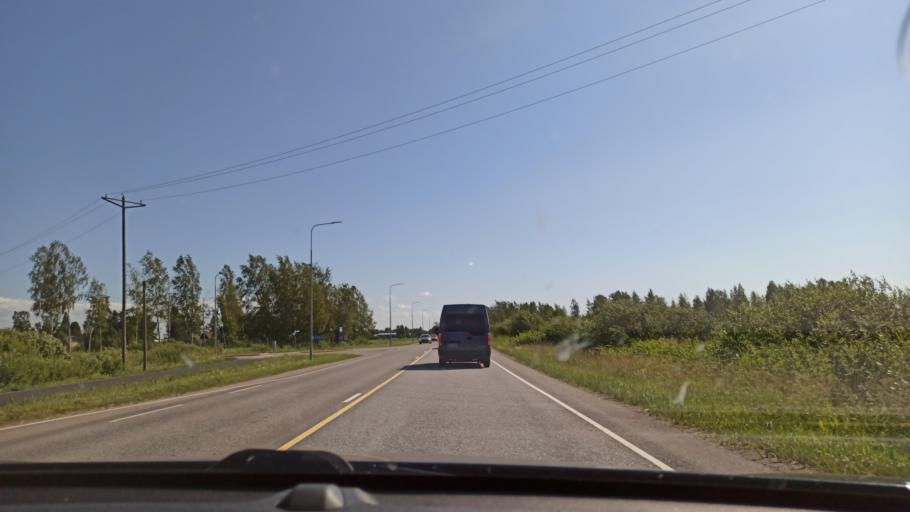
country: FI
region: Satakunta
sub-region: Pori
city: Pori
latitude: 61.5188
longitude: 21.8033
